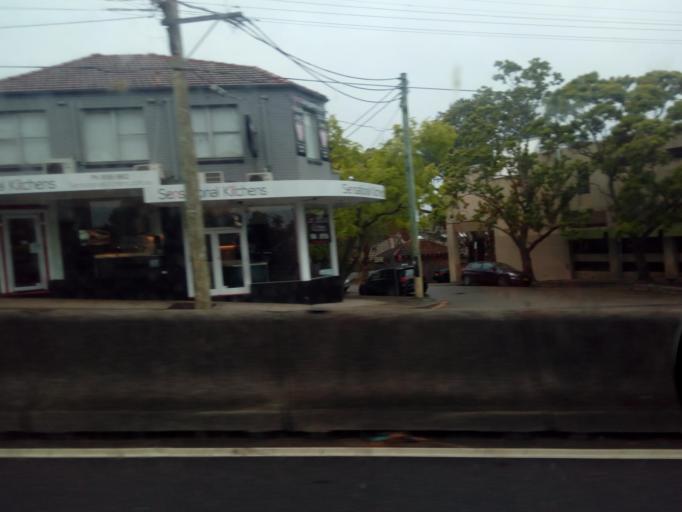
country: AU
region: New South Wales
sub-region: City of Sydney
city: Pymble
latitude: -33.7440
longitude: 151.1408
